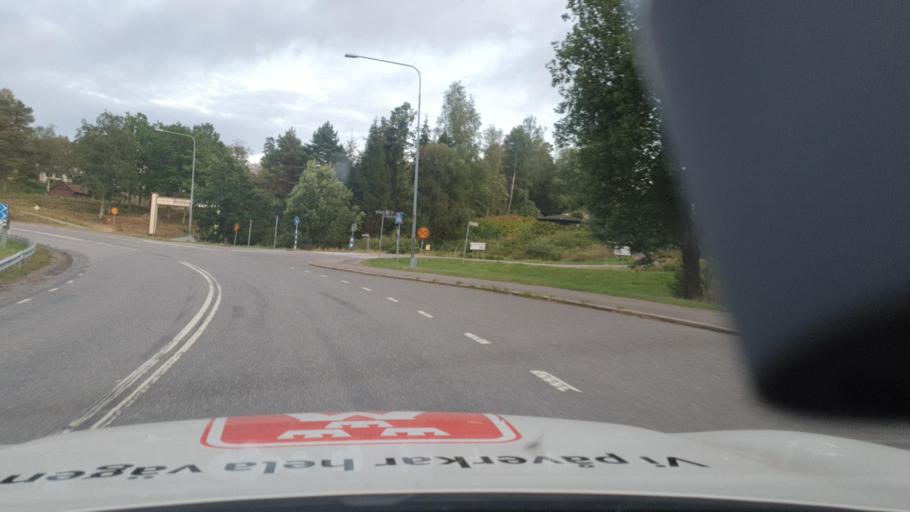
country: SE
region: Vaestra Goetaland
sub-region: Harryda Kommun
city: Hindas
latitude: 57.7065
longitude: 12.4684
